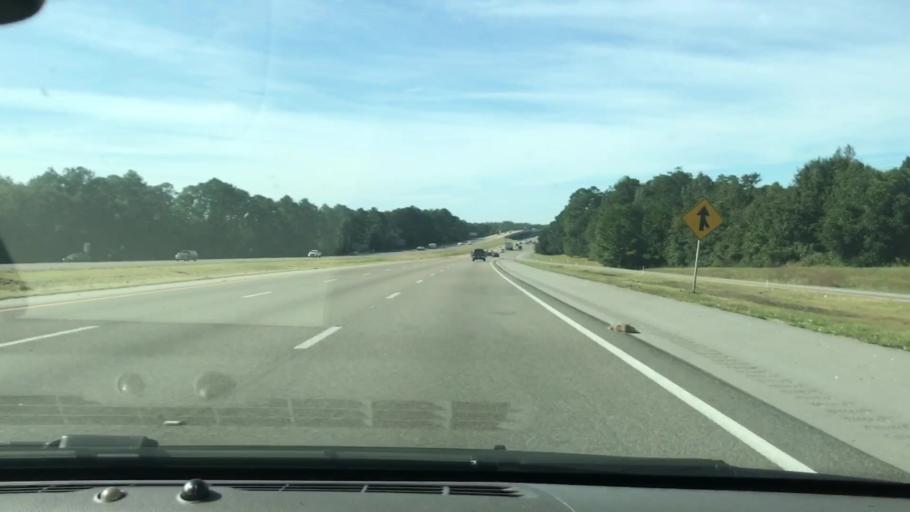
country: US
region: Mississippi
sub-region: Harrison County
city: D'Iberville
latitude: 30.4496
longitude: -88.9361
